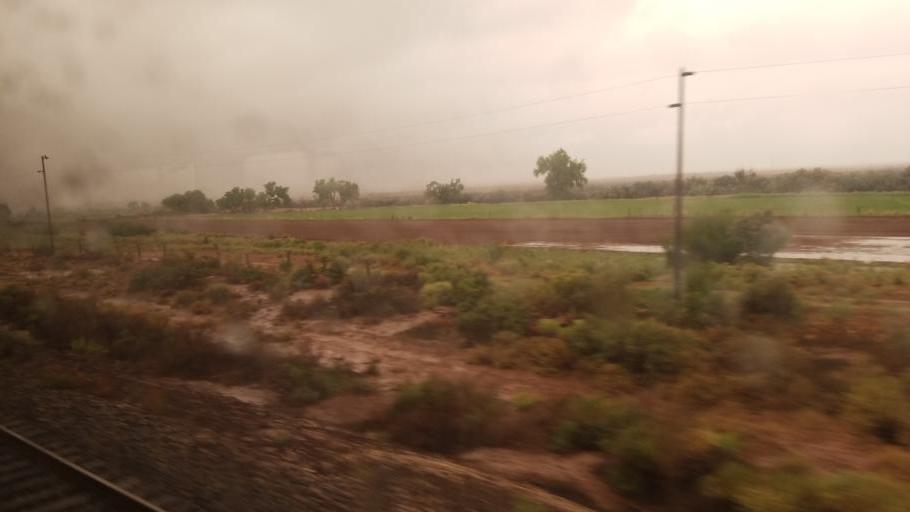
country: US
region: Arizona
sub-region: Navajo County
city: Joseph City
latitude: 34.9149
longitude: -110.2678
